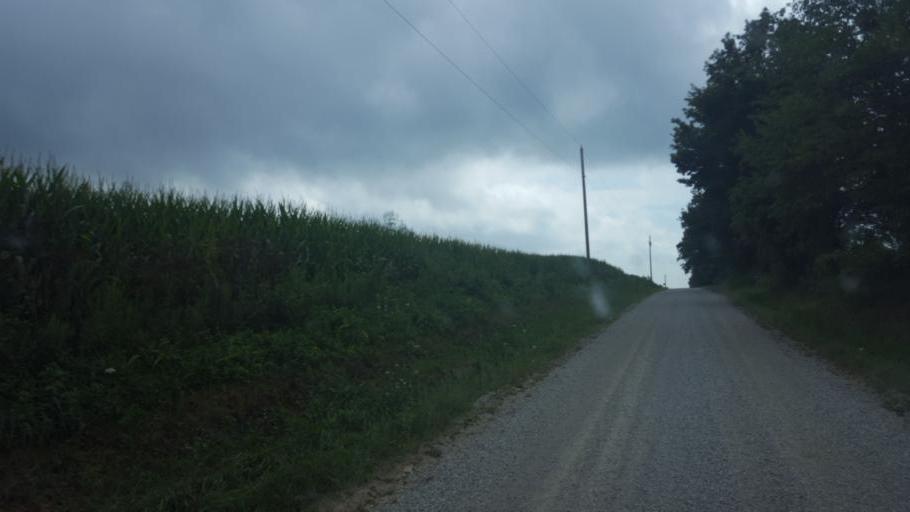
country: US
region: Ohio
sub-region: Morrow County
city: Mount Gilead
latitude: 40.5336
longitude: -82.6867
